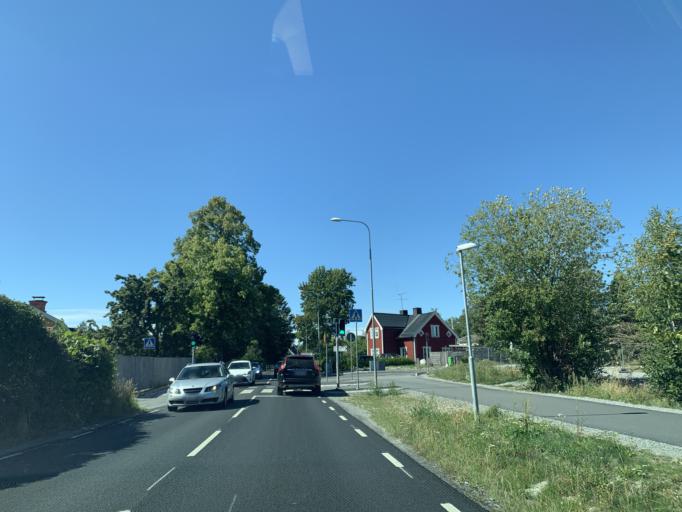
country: SE
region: Stockholm
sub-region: Ekero Kommun
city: Ekeroe
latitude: 59.2730
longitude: 17.7911
